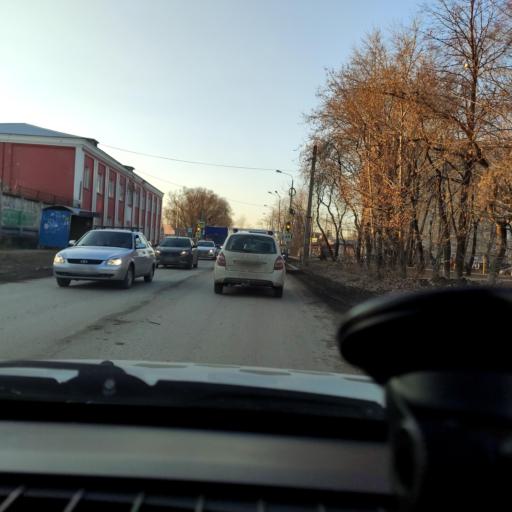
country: RU
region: Perm
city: Froly
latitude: 57.9667
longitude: 56.2660
